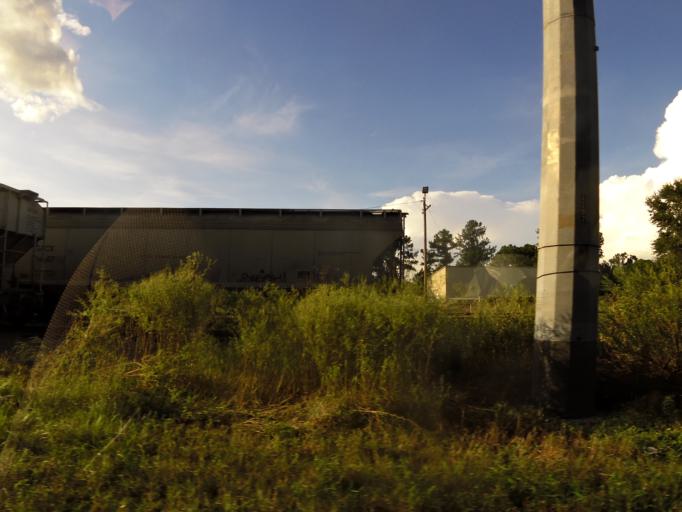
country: US
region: Georgia
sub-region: Lowndes County
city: Remerton
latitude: 30.8197
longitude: -83.3038
